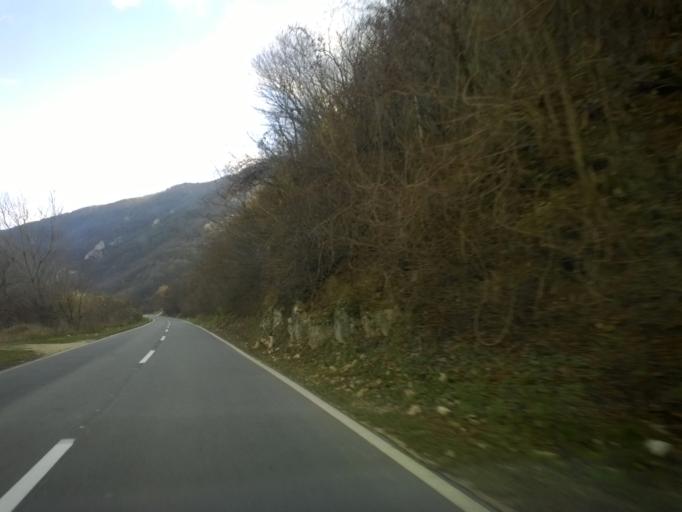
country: RO
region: Caras-Severin
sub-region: Comuna Pescari
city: Coronini
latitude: 44.6570
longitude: 21.7047
